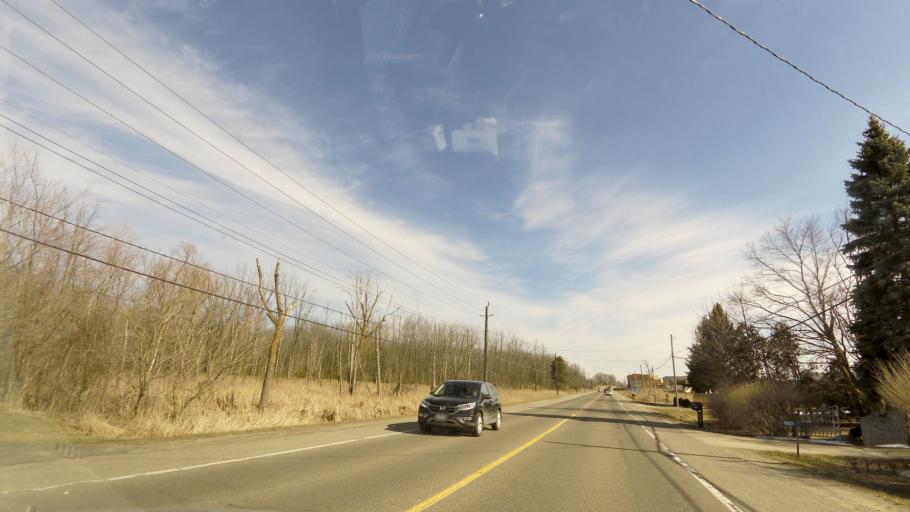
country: CA
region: Ontario
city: Burlington
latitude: 43.3432
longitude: -79.9118
